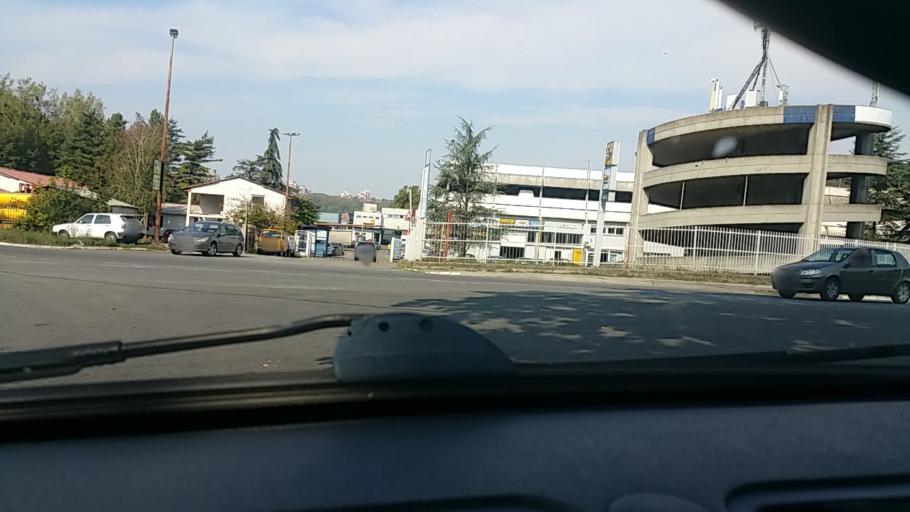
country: RS
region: Central Serbia
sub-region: Belgrade
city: Rakovica
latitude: 44.7344
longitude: 20.4476
